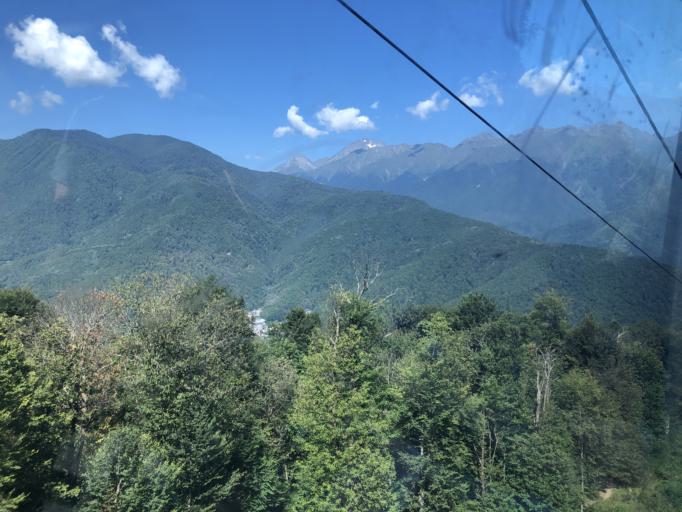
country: RU
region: Krasnodarskiy
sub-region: Sochi City
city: Krasnaya Polyana
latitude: 43.6728
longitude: 40.2612
